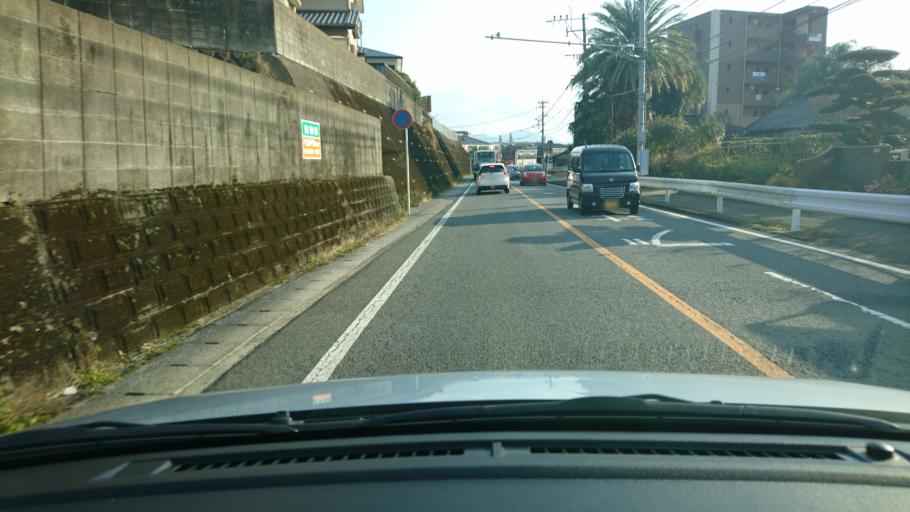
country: JP
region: Miyazaki
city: Miyazaki-shi
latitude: 31.8855
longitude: 131.4089
